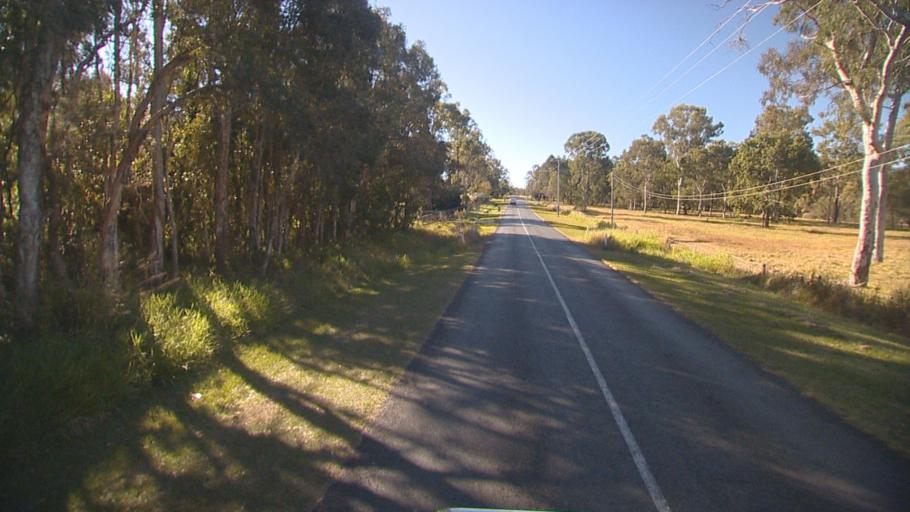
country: AU
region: Queensland
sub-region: Logan
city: North Maclean
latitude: -27.7532
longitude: 153.0137
